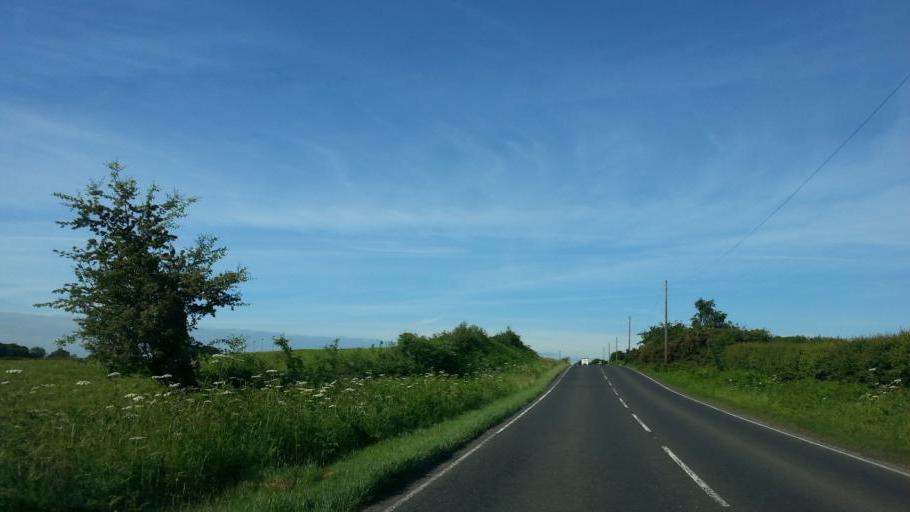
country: GB
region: England
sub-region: Nottinghamshire
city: Arnold
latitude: 53.0376
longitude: -1.1249
